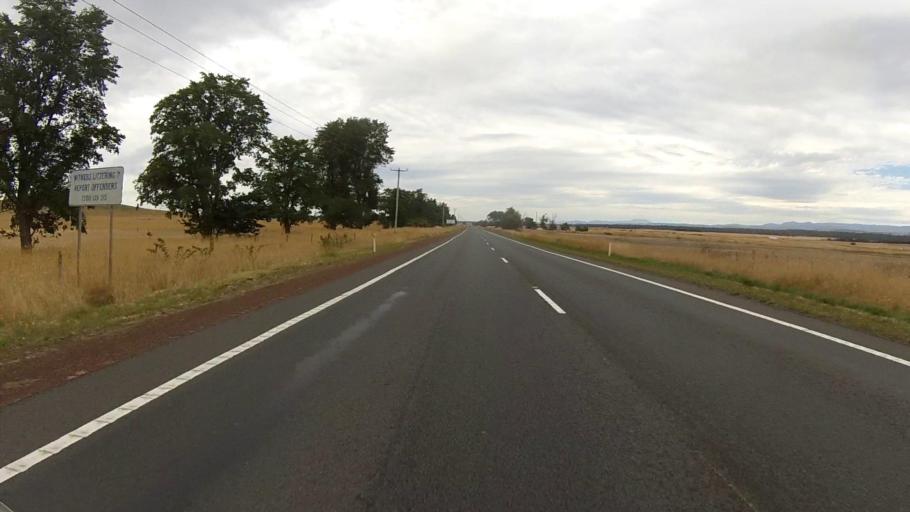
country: AU
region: Tasmania
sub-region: Northern Midlands
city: Evandale
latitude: -41.9038
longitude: 147.4778
